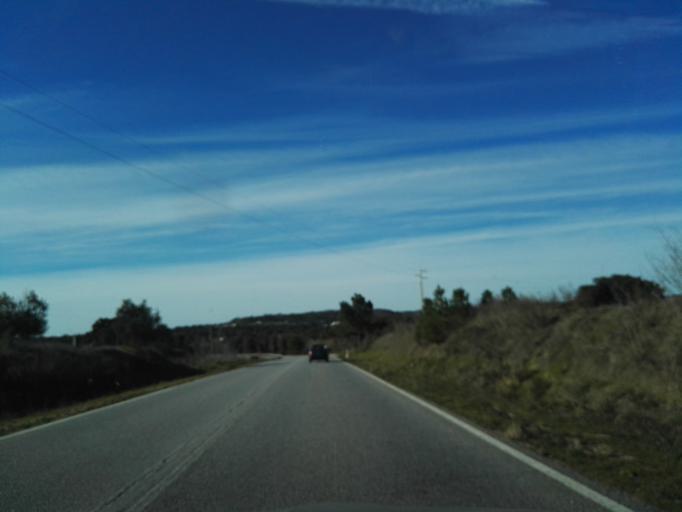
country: PT
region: Santarem
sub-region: Abrantes
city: Alferrarede
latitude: 39.4678
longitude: -8.0597
